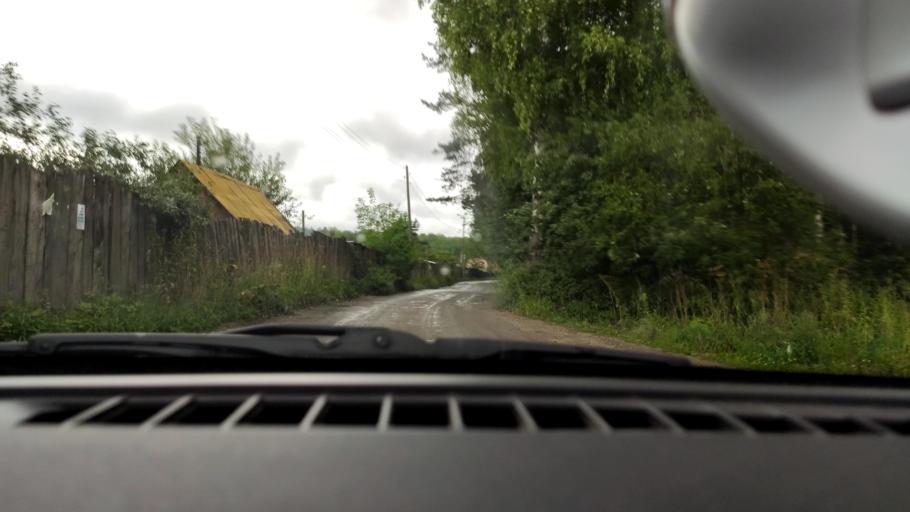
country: RU
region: Perm
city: Overyata
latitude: 58.0522
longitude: 55.9874
